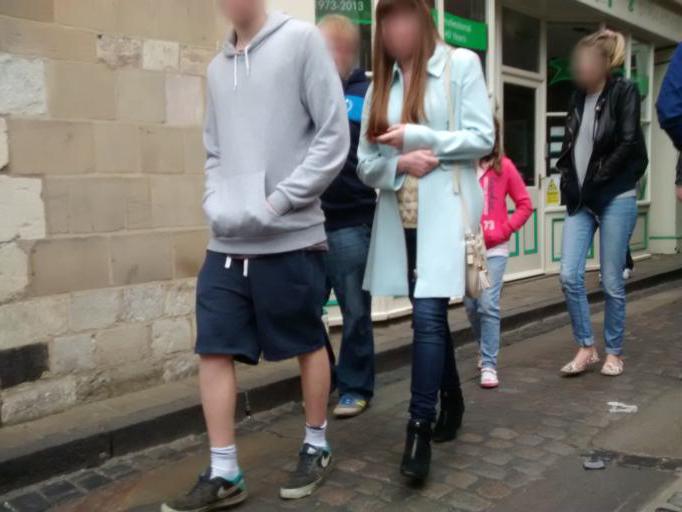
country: GB
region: England
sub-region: City of York
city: York
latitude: 53.9597
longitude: -1.0805
